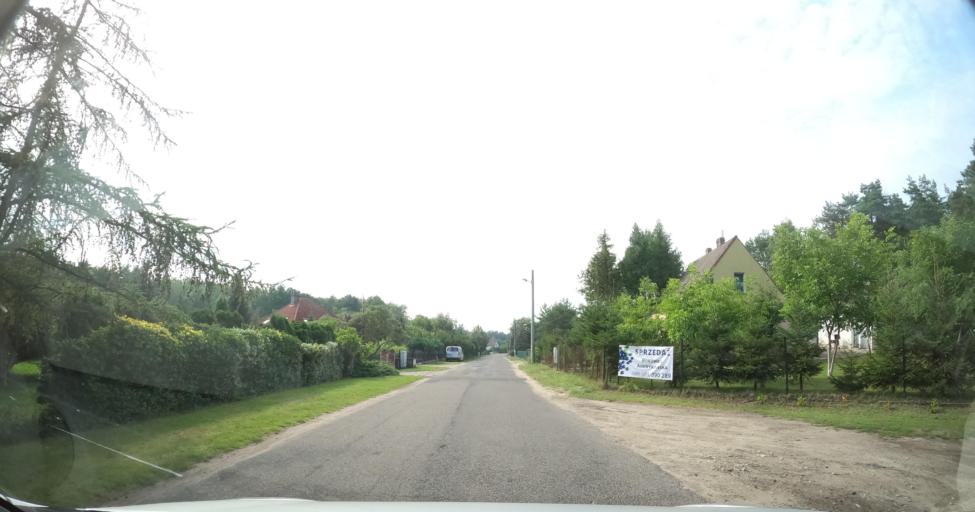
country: PL
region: West Pomeranian Voivodeship
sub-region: Powiat goleniowski
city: Goleniow
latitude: 53.5040
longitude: 14.8806
